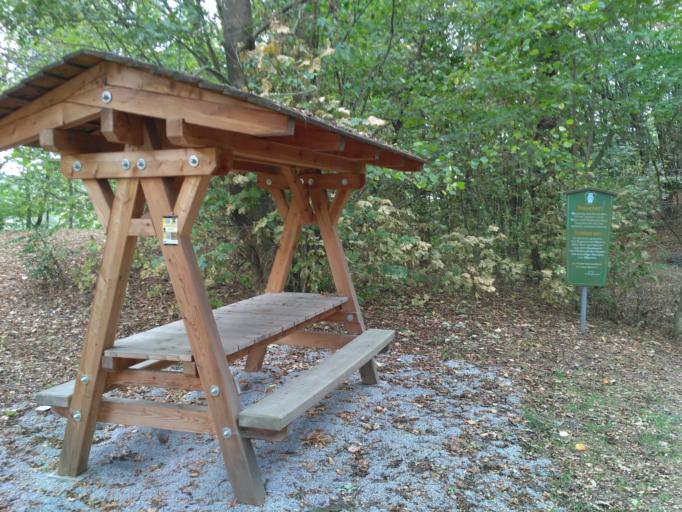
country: DE
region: Saxony
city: Kirschau
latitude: 51.0891
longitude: 14.4313
